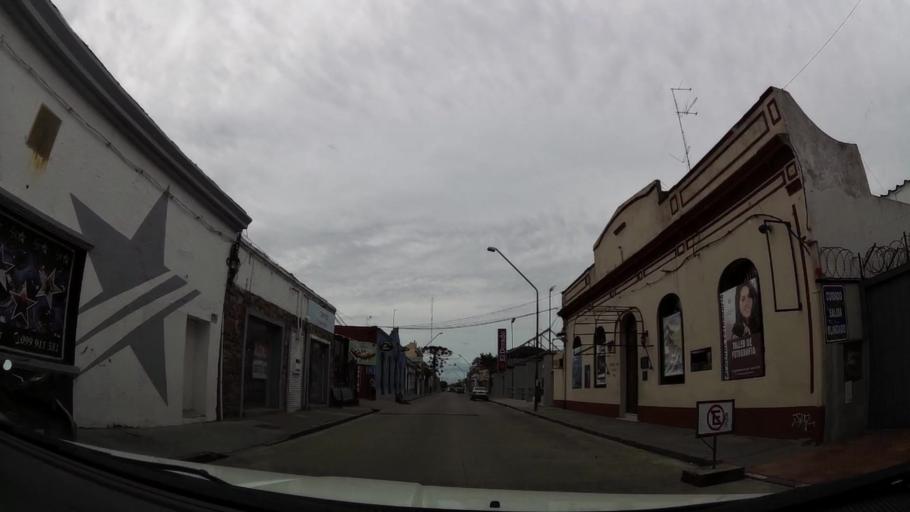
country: UY
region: Maldonado
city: Maldonado
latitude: -34.9082
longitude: -54.9598
